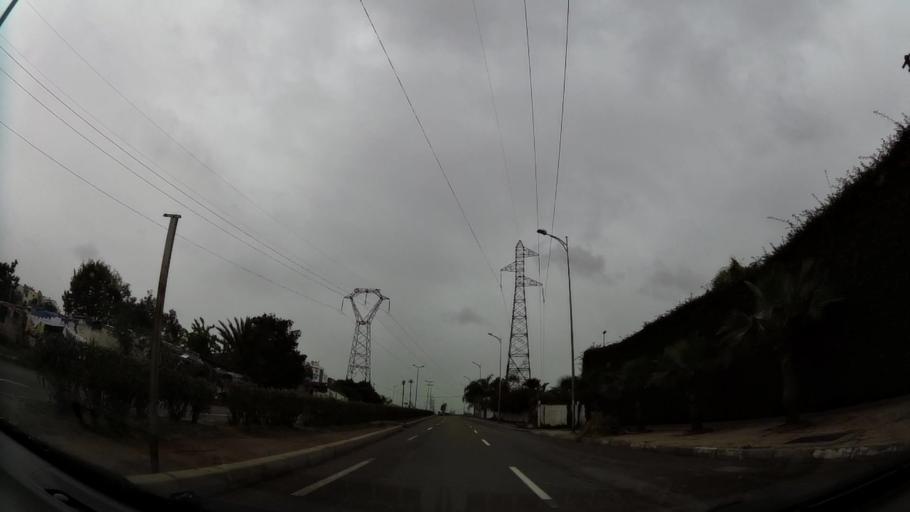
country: MA
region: Grand Casablanca
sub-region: Casablanca
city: Casablanca
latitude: 33.5368
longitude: -7.6177
